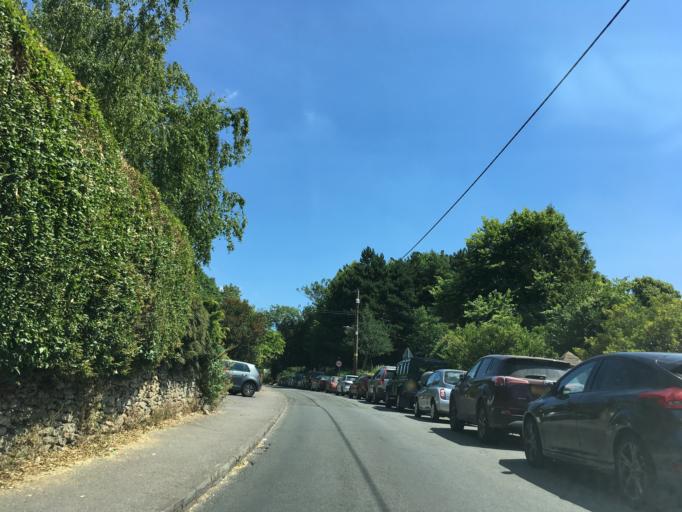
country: GB
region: England
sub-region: Gloucestershire
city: Stroud
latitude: 51.7425
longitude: -2.2011
